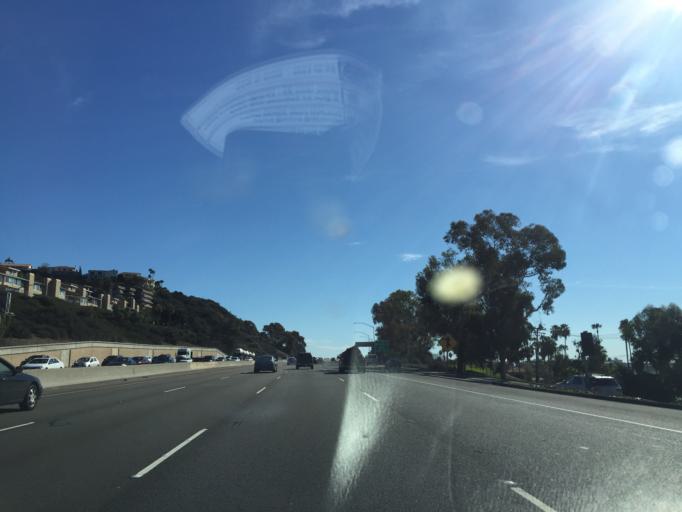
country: US
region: California
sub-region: Orange County
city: San Clemente
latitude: 33.4253
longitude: -117.6095
